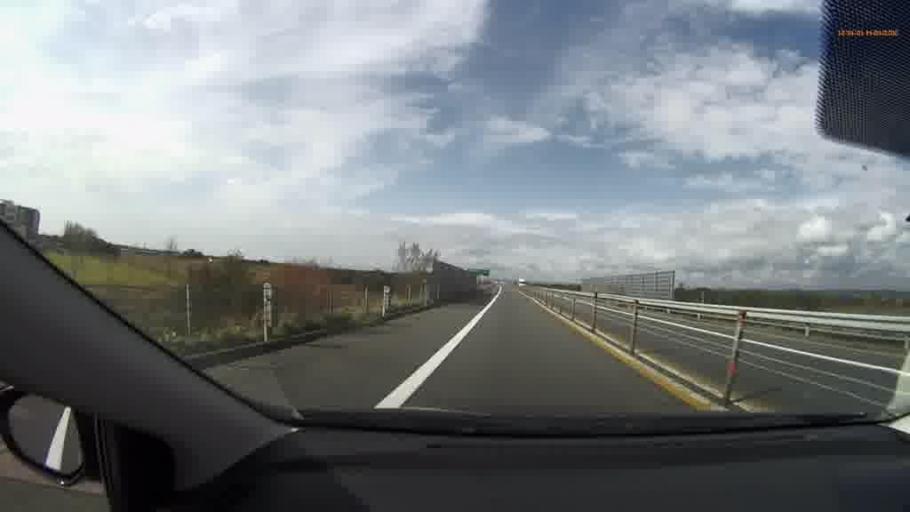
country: JP
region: Hokkaido
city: Kushiro
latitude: 43.0365
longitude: 144.3582
